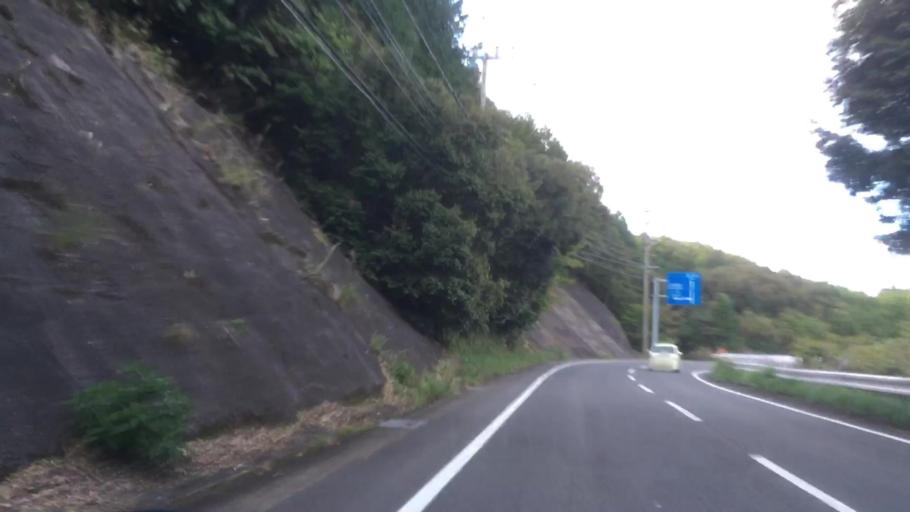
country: JP
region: Nagasaki
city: Sasebo
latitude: 32.9717
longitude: 129.6974
